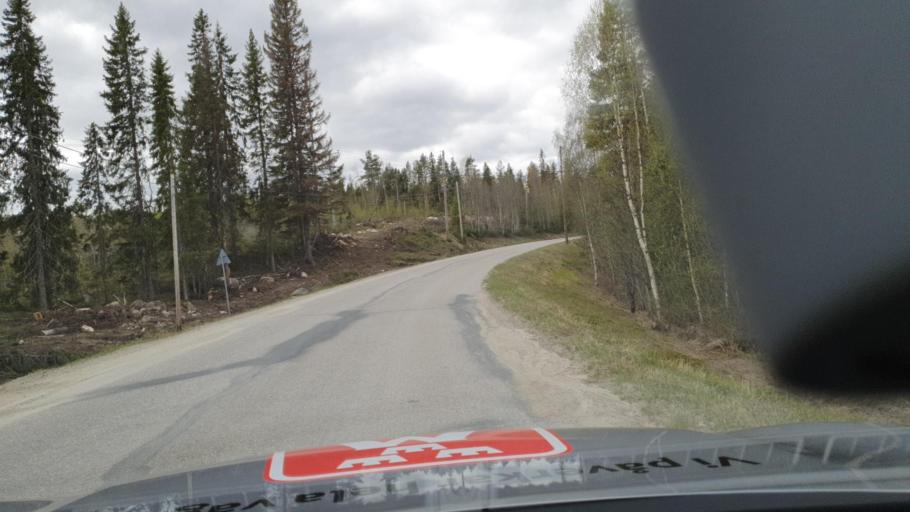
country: SE
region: Vaesternorrland
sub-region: OErnskoeldsviks Kommun
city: Ornskoldsvik
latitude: 63.6330
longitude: 18.7937
